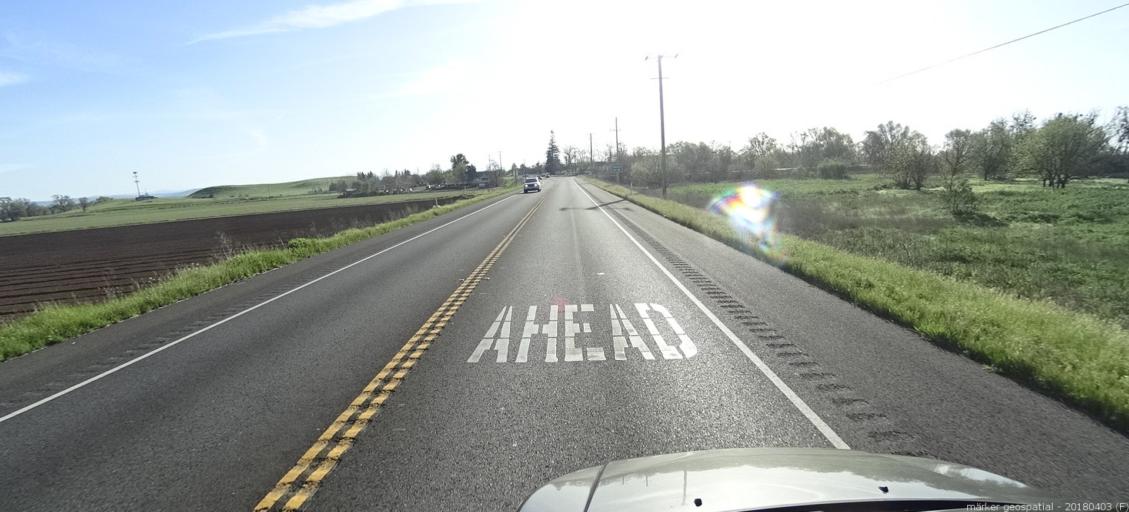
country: US
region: California
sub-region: Sacramento County
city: Rancho Murieta
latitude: 38.4930
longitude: -121.1641
